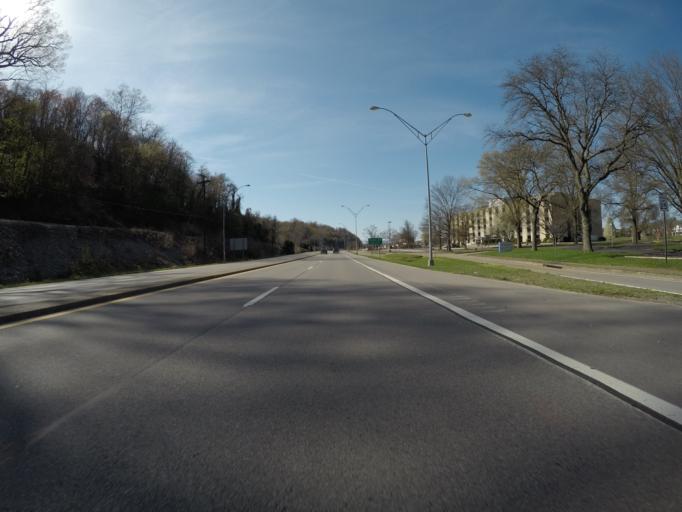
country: US
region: West Virginia
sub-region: Kanawha County
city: Charleston
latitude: 38.3361
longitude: -81.6260
